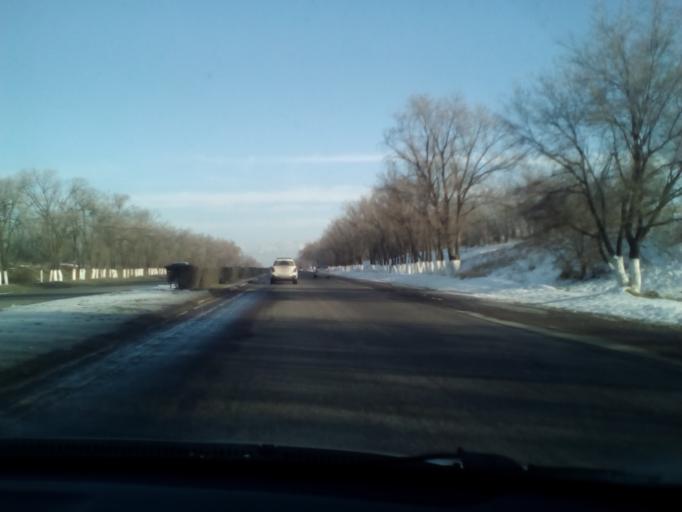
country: KZ
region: Almaty Oblysy
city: Burunday
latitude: 43.2212
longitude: 76.4454
